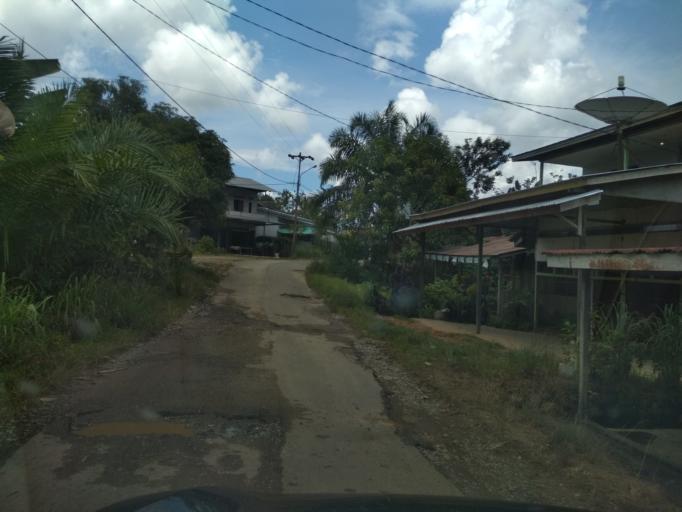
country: ID
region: West Kalimantan
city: Bengkayang
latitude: 0.7475
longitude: 110.1060
